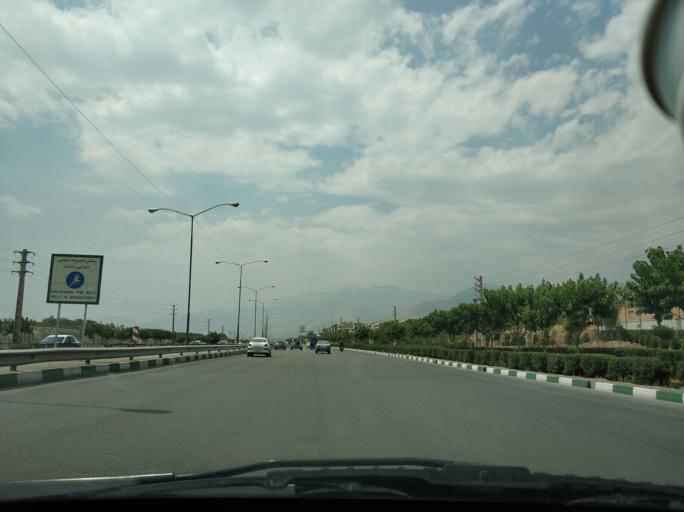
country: IR
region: Tehran
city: Tajrish
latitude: 35.7636
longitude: 51.5678
